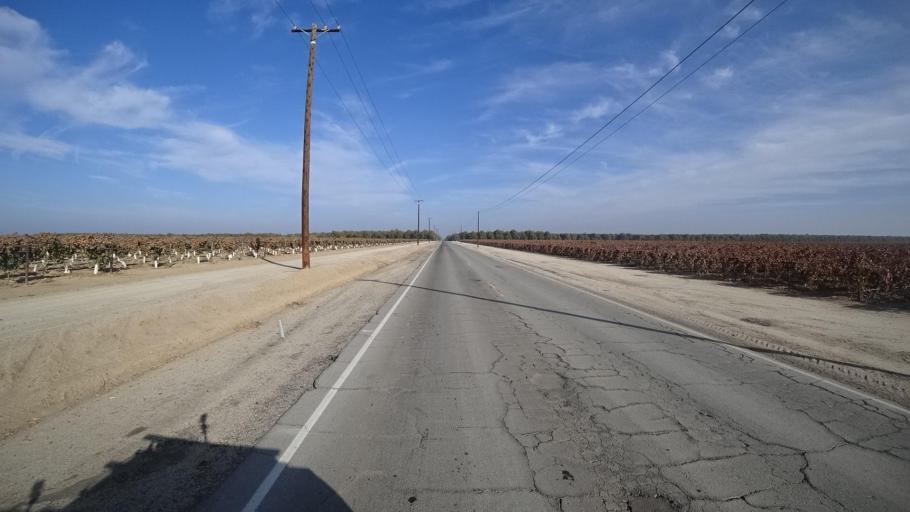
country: US
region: California
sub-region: Kern County
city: McFarland
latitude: 35.6132
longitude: -119.2043
